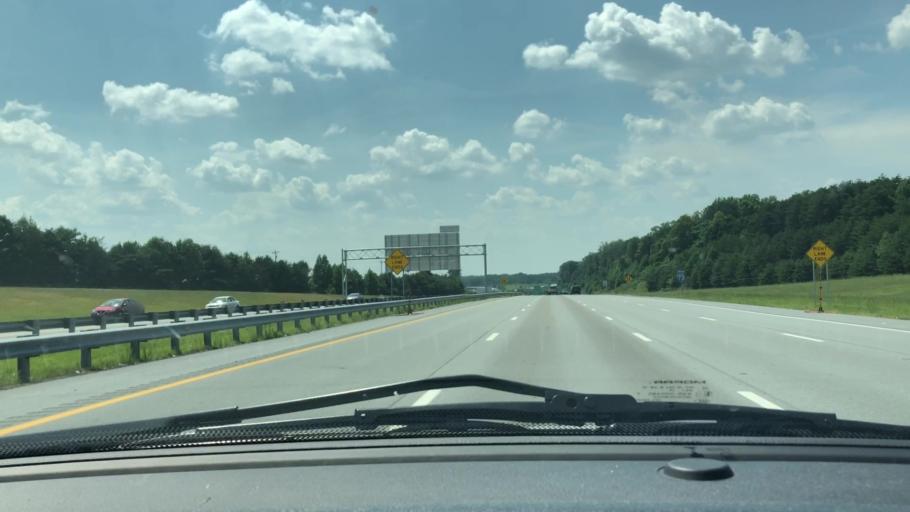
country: US
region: North Carolina
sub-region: Guilford County
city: Summerfield
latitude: 36.1198
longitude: -79.9163
